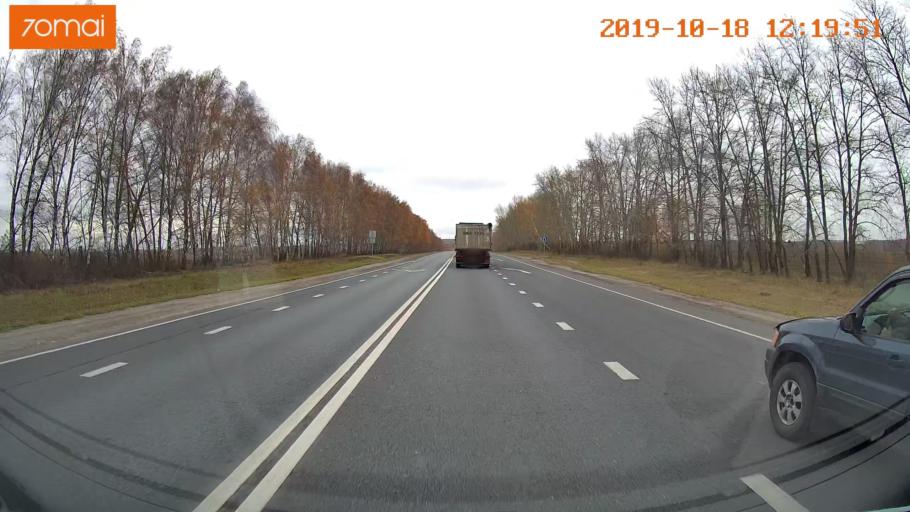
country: RU
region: Rjazan
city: Zakharovo
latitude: 54.4884
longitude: 39.4730
